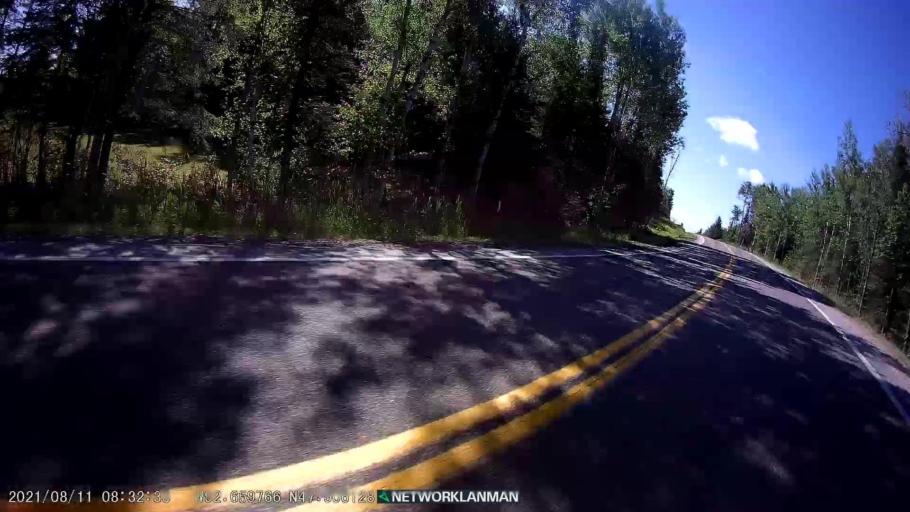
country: US
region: Minnesota
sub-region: Saint Louis County
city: Mountain Iron
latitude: 47.9058
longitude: -92.6601
